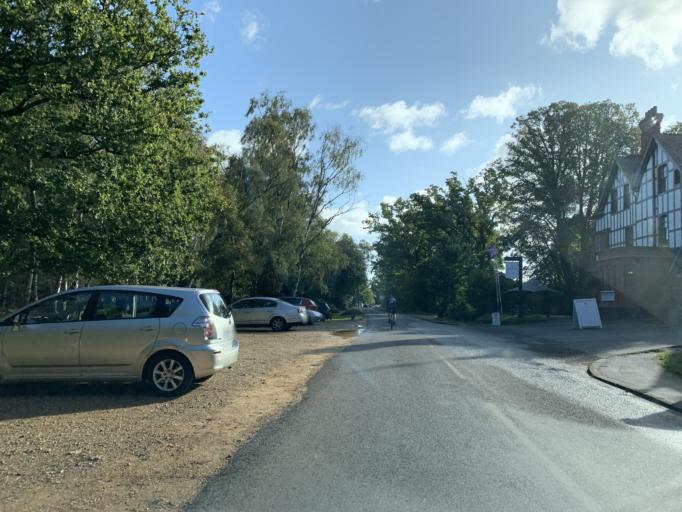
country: GB
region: England
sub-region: Hampshire
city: Brockenhurst
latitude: 50.8227
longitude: -1.5860
